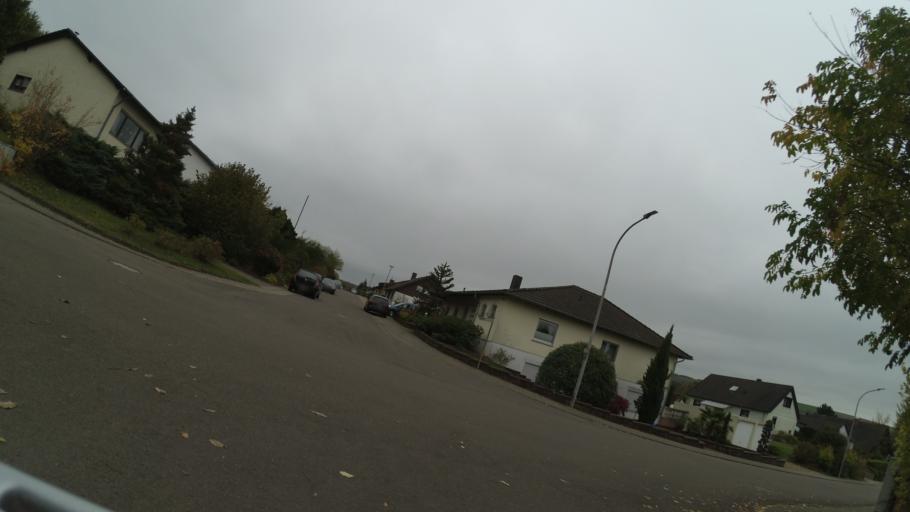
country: DE
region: Saarland
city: Blieskastel
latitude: 49.2410
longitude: 7.2771
